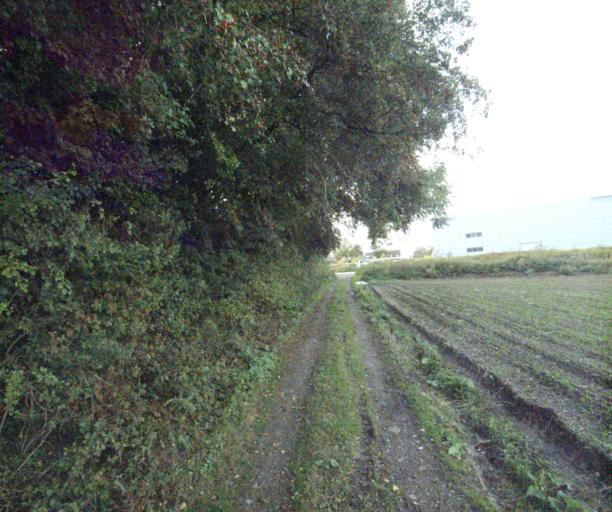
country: FR
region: Nord-Pas-de-Calais
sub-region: Departement du Nord
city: Hallennes-lez-Haubourdin
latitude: 50.6260
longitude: 2.9695
